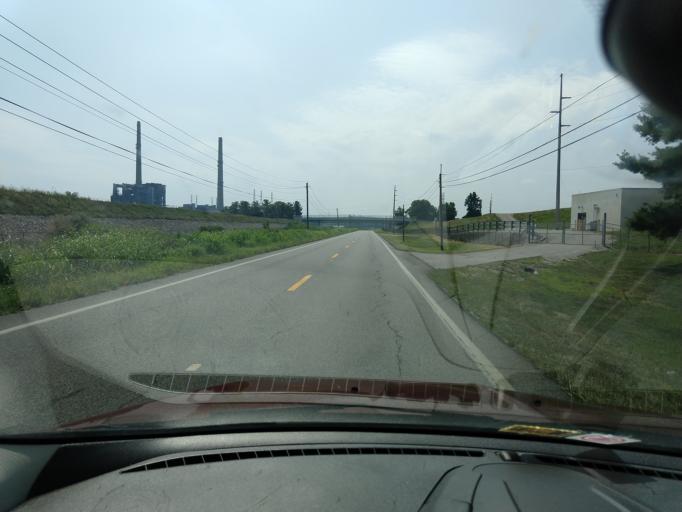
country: US
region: West Virginia
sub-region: Mason County
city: New Haven
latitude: 38.9714
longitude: -81.9338
